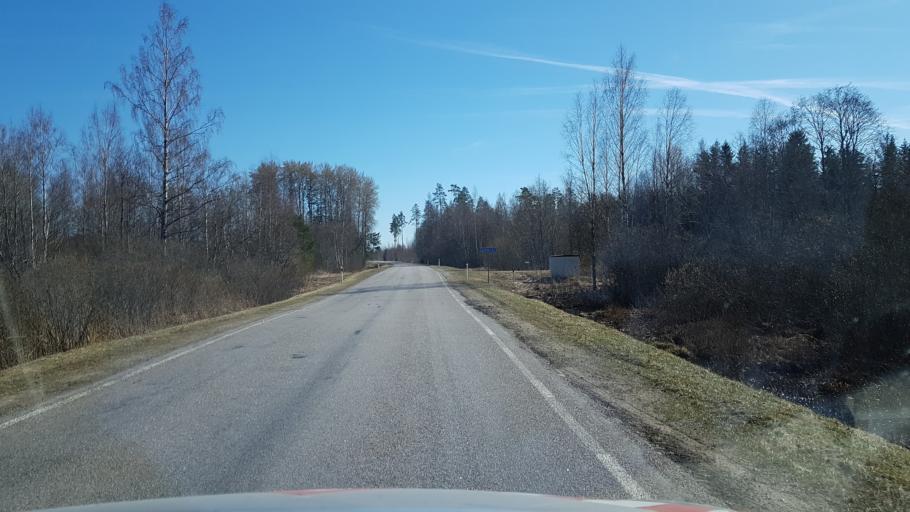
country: EE
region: Laeaene-Virumaa
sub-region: Vinni vald
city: Vinni
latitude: 59.2489
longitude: 26.6883
